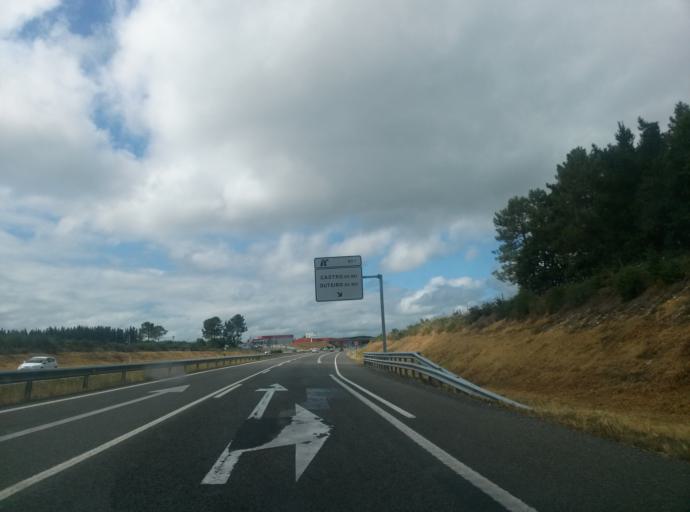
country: ES
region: Galicia
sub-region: Provincia de Lugo
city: Outeiro de Rei
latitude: 43.1021
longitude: -7.6007
